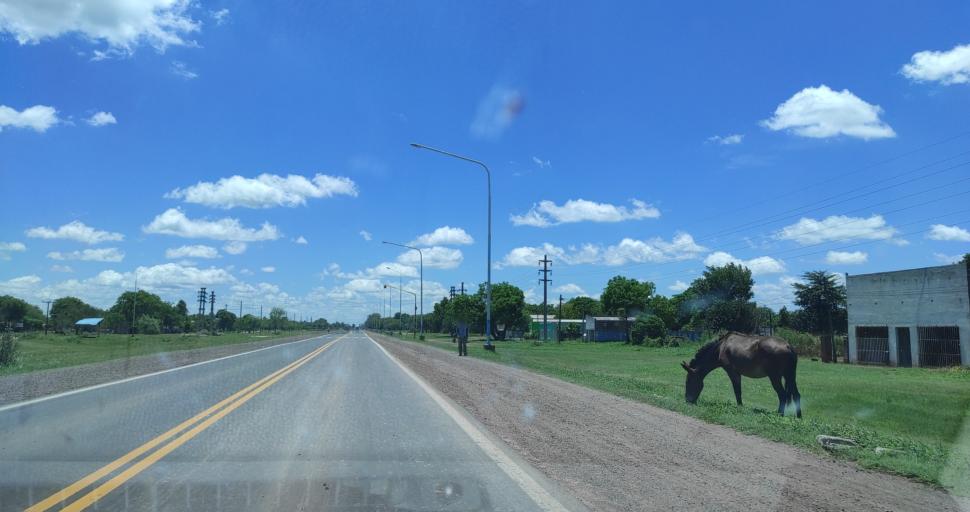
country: AR
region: Chaco
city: Campo Largo
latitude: -26.8107
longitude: -60.8410
